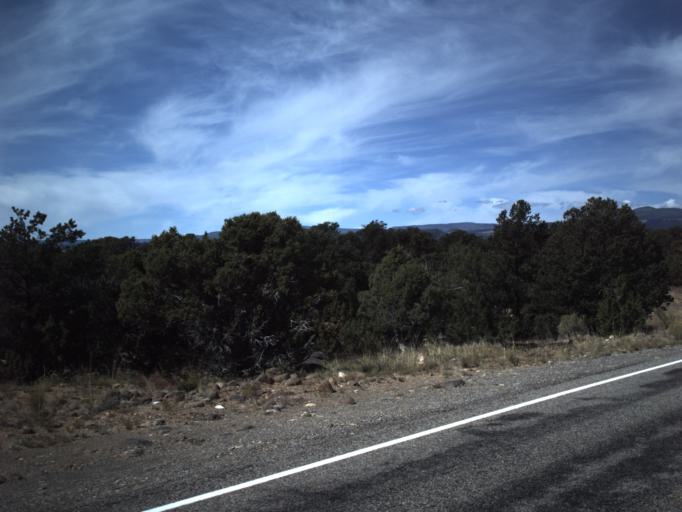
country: US
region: Utah
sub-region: Wayne County
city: Loa
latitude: 37.8603
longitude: -111.4372
